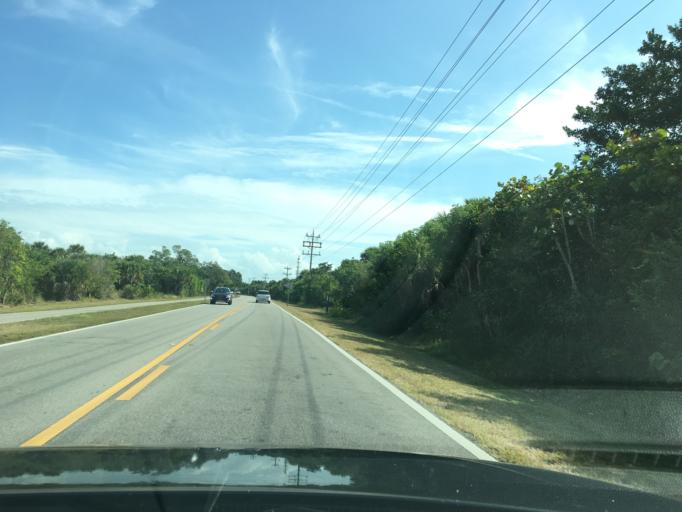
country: US
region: Florida
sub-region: Lee County
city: Saint James City
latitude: 26.4385
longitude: -82.0923
